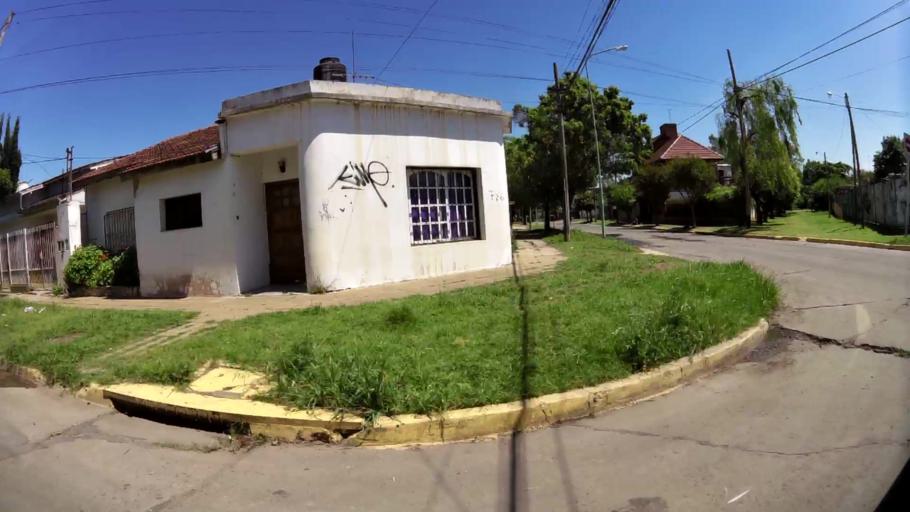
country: AR
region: Buenos Aires
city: Ituzaingo
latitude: -34.6714
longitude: -58.6869
